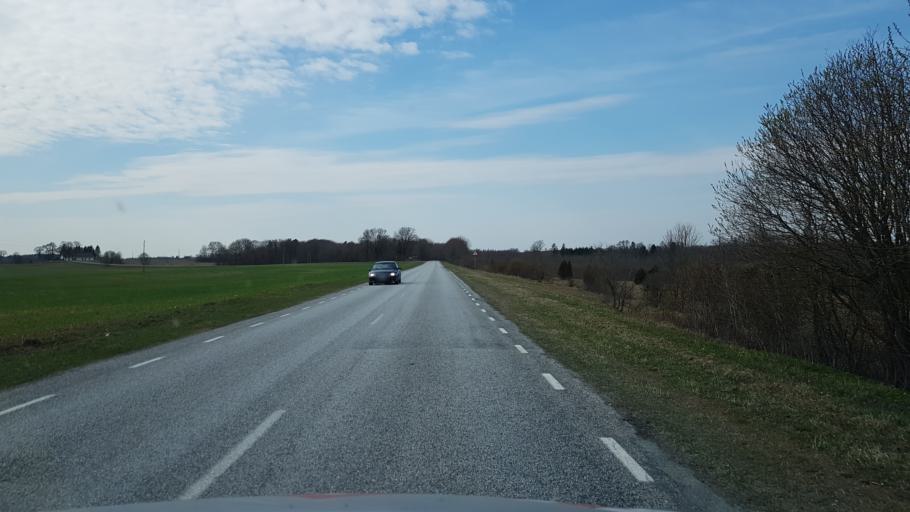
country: EE
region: Laeaene-Virumaa
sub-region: Haljala vald
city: Haljala
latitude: 59.4735
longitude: 26.1681
